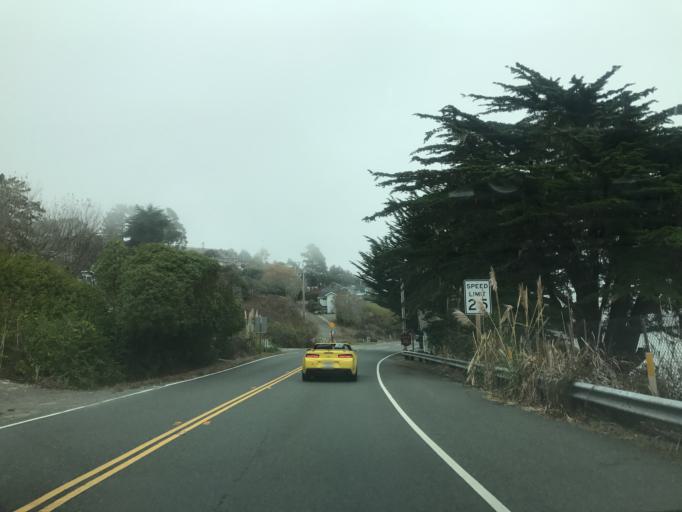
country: US
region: California
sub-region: Sonoma County
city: Monte Rio
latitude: 38.4507
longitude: -123.1210
